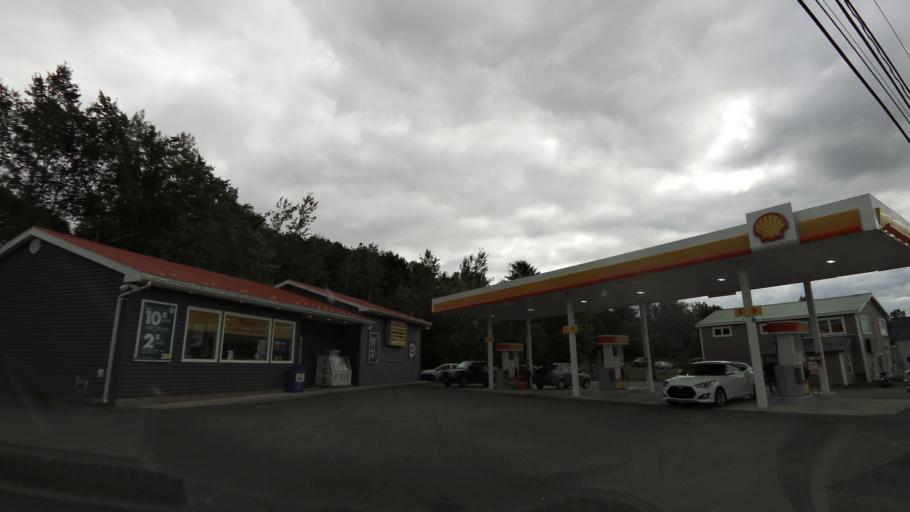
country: CA
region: New Brunswick
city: Hampton
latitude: 45.5241
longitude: -65.8292
